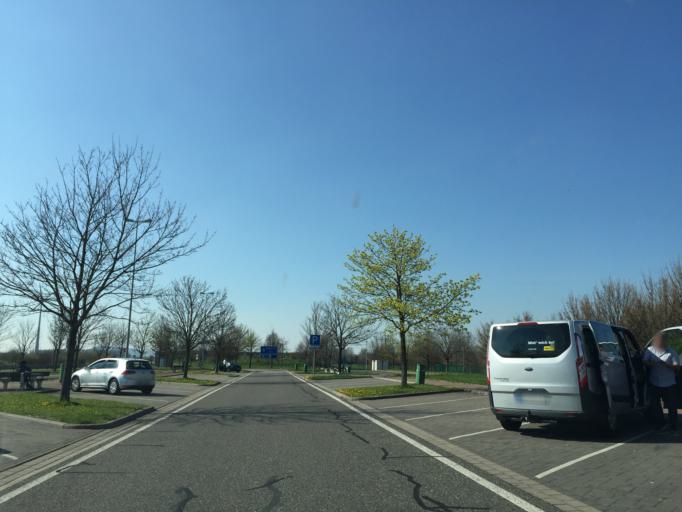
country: DE
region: Thuringia
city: Horselgau
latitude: 50.9129
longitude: 10.5867
